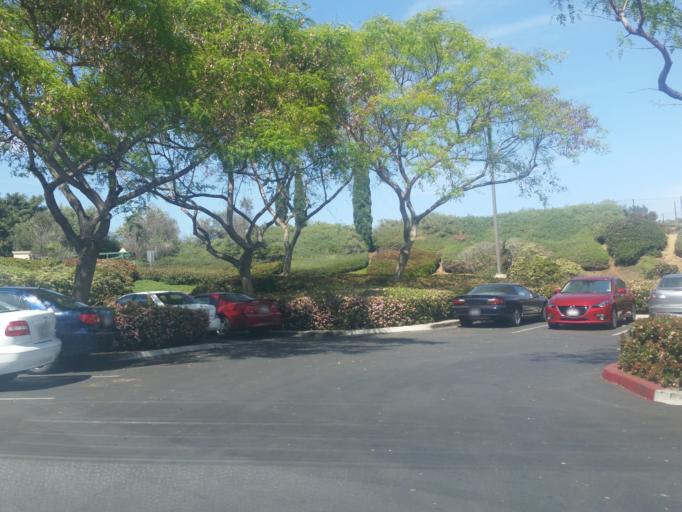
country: US
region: California
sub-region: San Diego County
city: Carlsbad
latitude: 33.1283
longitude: -117.3215
